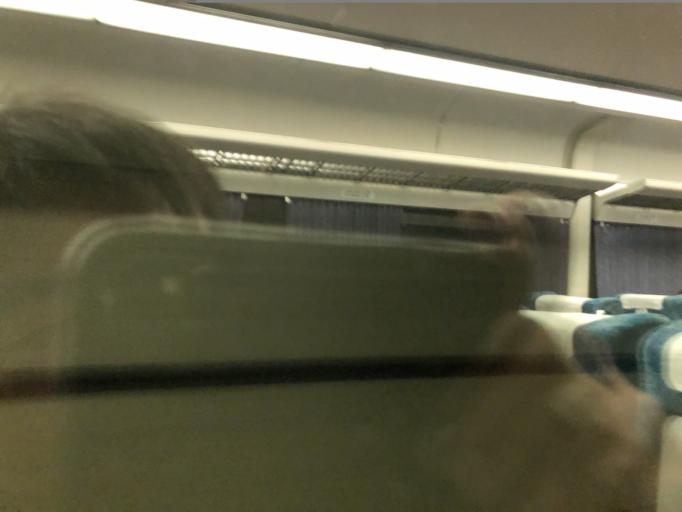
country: JP
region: Kochi
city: Nakamura
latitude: 33.0721
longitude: 133.1039
